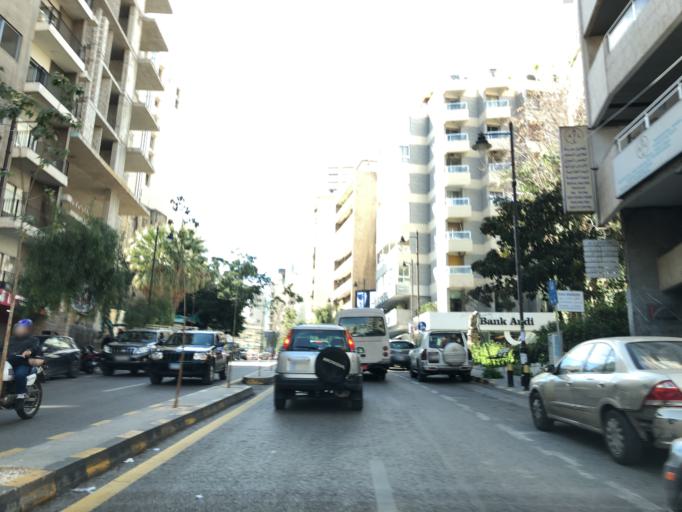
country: LB
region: Beyrouth
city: Beirut
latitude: 33.8879
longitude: 35.5236
